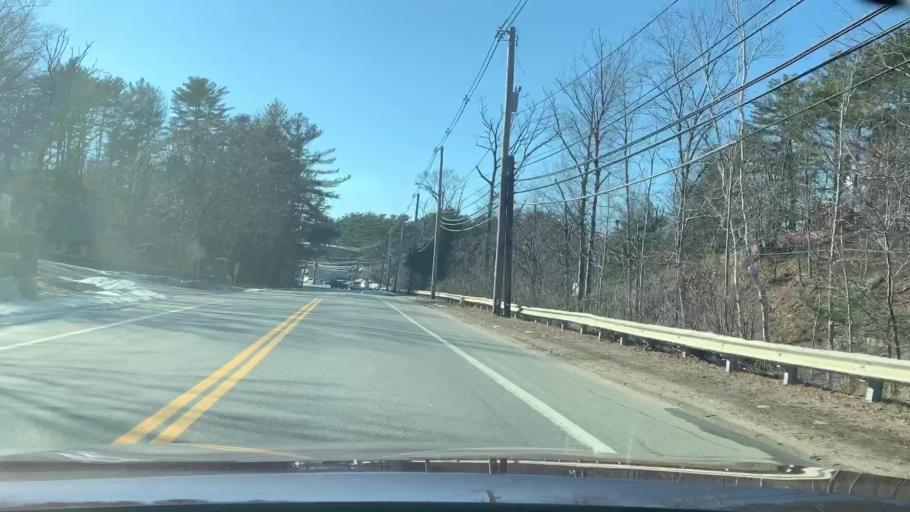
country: US
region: Massachusetts
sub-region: Essex County
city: Gloucester
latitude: 42.6157
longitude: -70.6968
